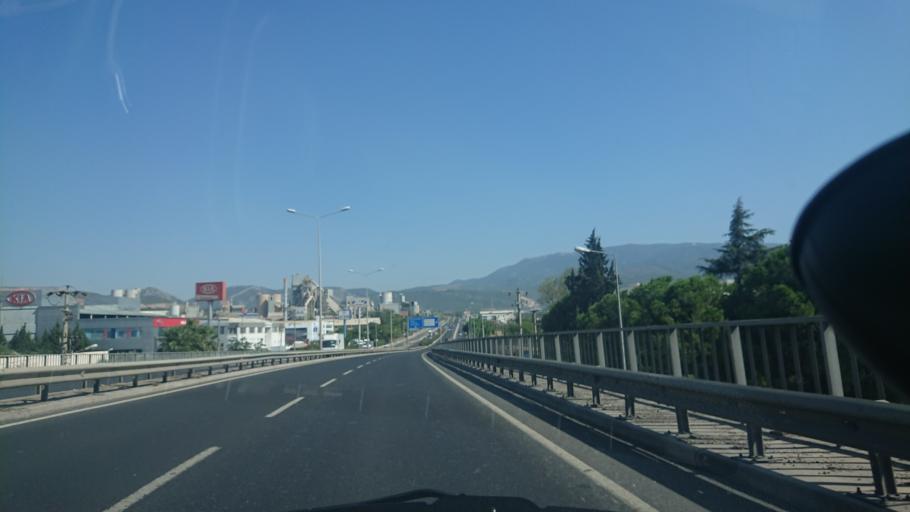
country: TR
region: Izmir
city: Bornova
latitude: 38.4572
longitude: 27.2522
